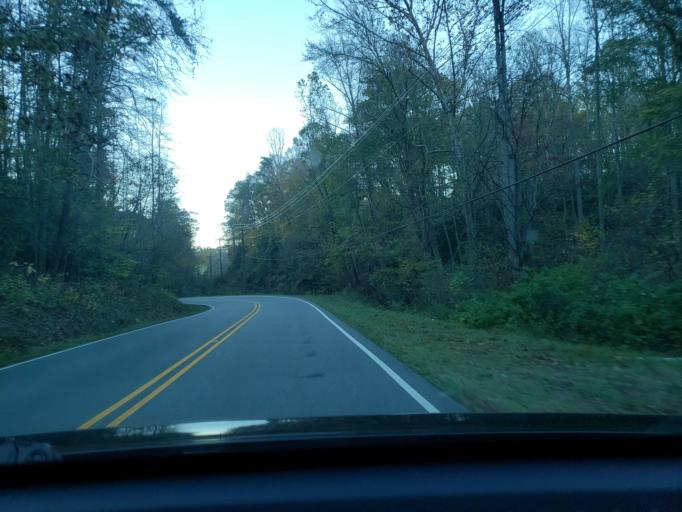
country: US
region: North Carolina
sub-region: Stokes County
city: Danbury
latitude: 36.3859
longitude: -80.1892
